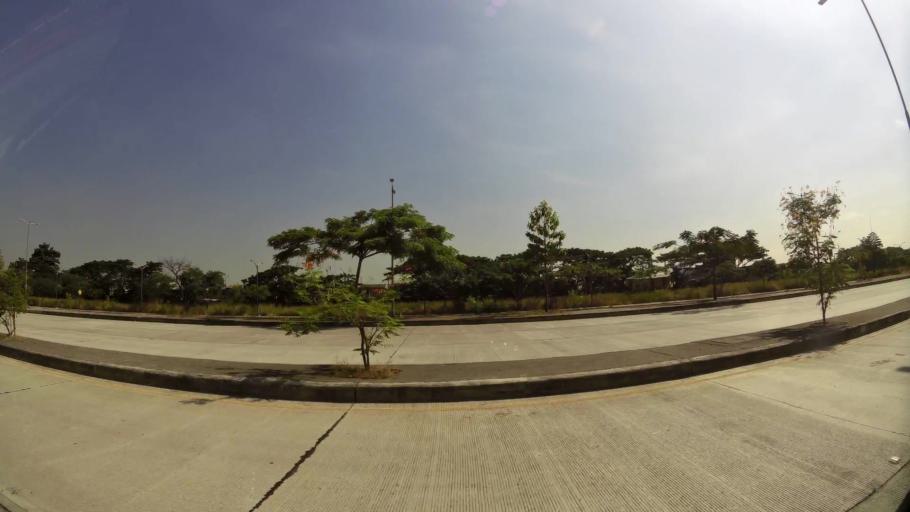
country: EC
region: Guayas
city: Eloy Alfaro
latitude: -2.1023
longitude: -79.9078
